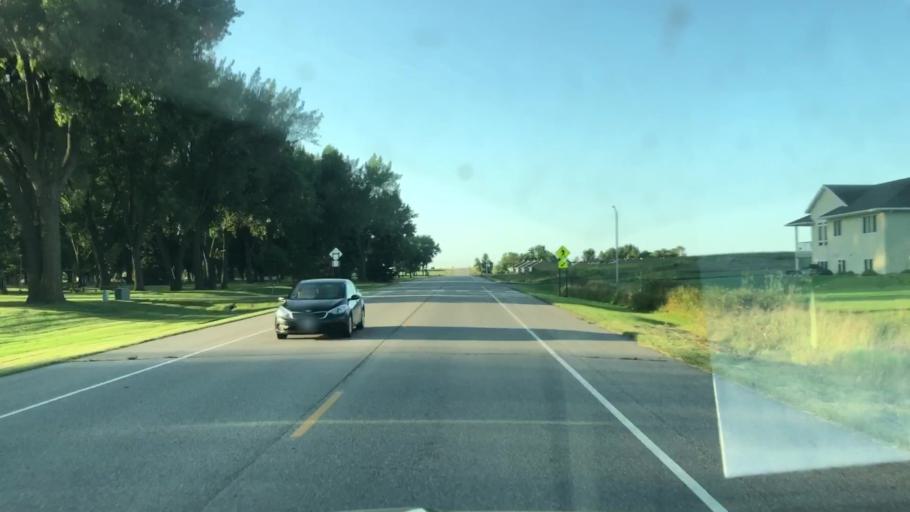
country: US
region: Minnesota
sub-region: Nobles County
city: Worthington
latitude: 43.6104
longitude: -95.6366
